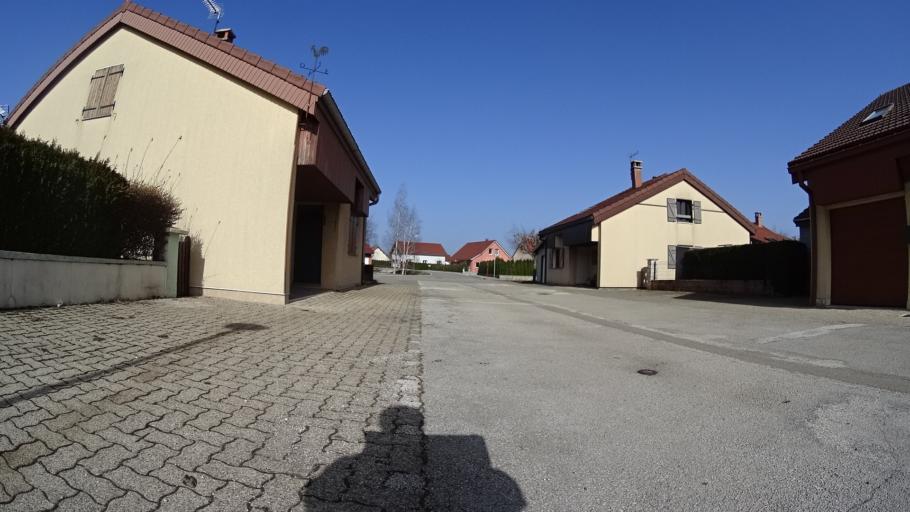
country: FR
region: Franche-Comte
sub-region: Departement du Doubs
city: Frasne
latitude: 46.8506
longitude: 6.1609
